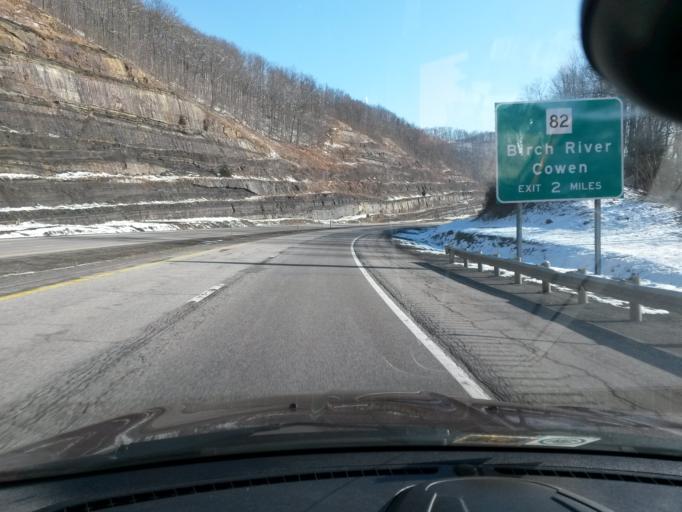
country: US
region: West Virginia
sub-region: Nicholas County
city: Craigsville
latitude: 38.4735
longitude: -80.7786
